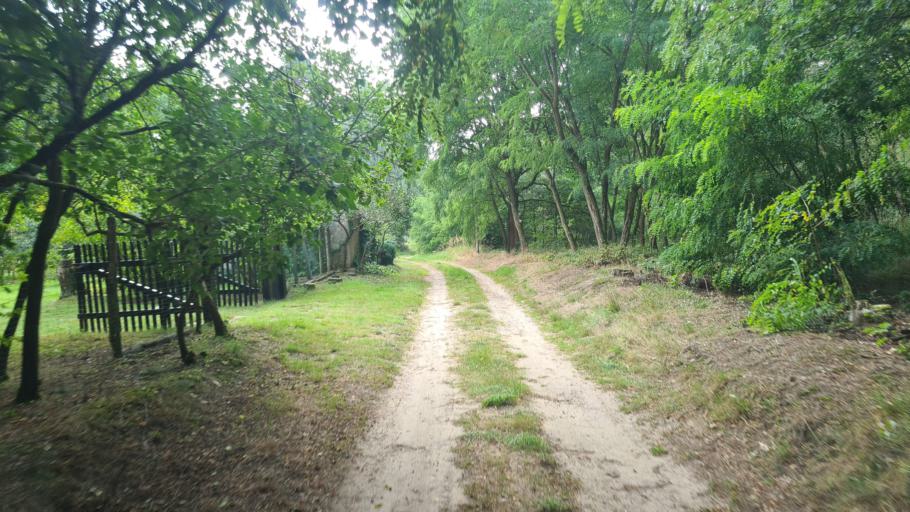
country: DE
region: Brandenburg
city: Schonewalde
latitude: 51.7483
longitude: 13.5990
